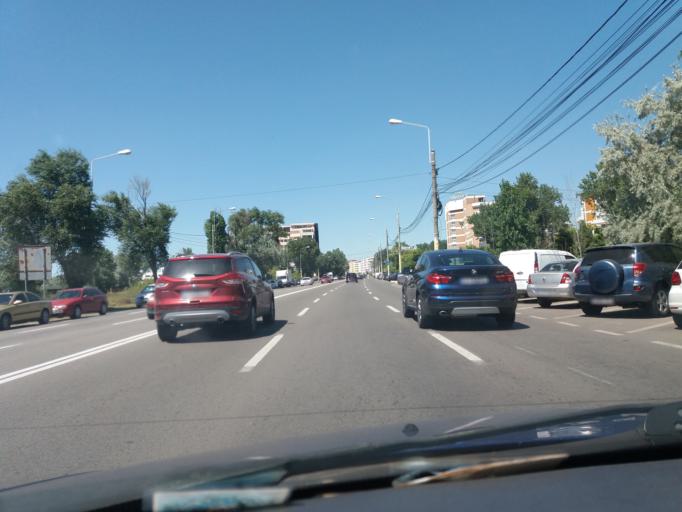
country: RO
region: Constanta
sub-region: Municipiul Constanta
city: Palazu Mare
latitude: 44.2601
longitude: 28.6183
